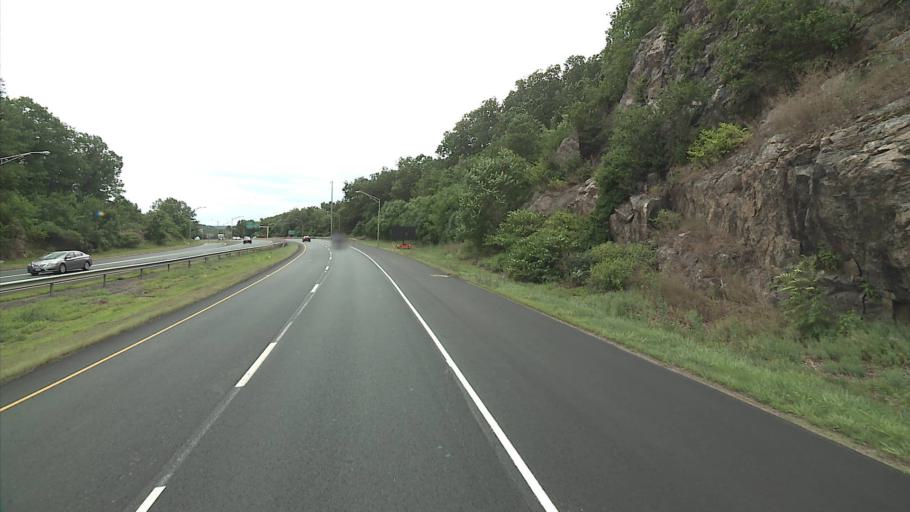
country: US
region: Connecticut
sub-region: New Haven County
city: Naugatuck
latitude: 41.5174
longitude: -73.0494
